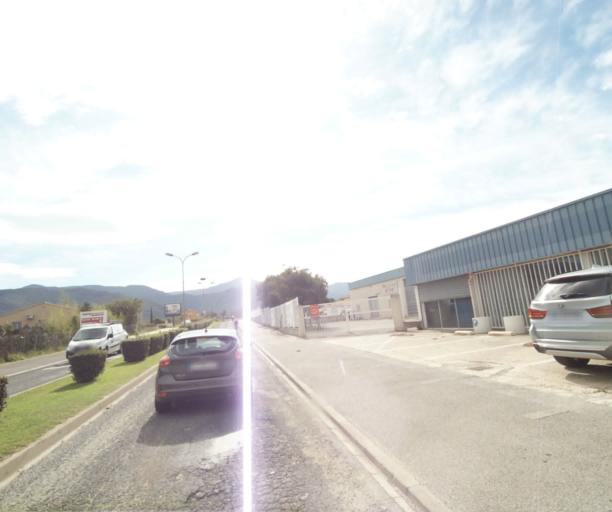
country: FR
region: Languedoc-Roussillon
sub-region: Departement des Pyrenees-Orientales
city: Argelers
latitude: 42.5525
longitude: 3.0109
